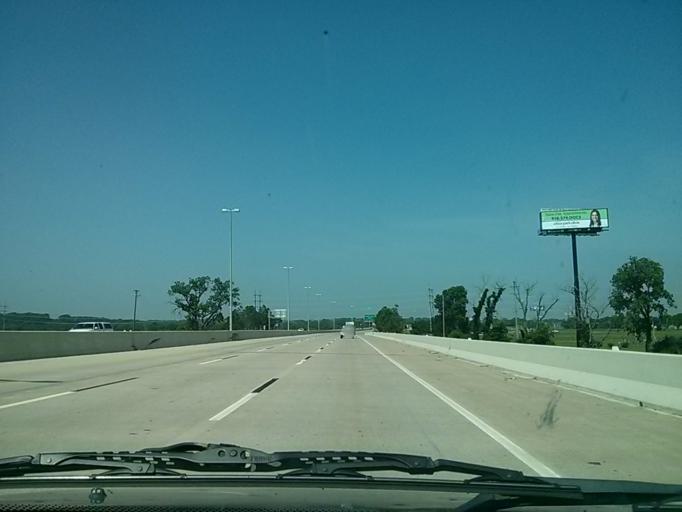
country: US
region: Oklahoma
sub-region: Tulsa County
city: Jenks
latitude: 36.0181
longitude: -95.9538
